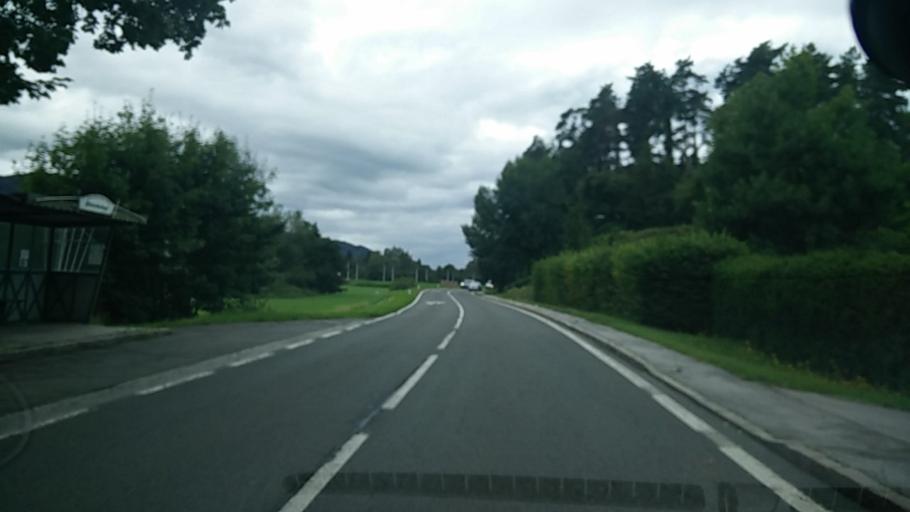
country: AT
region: Carinthia
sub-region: Politischer Bezirk Klagenfurt Land
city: Maria Worth
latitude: 46.6211
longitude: 14.1903
